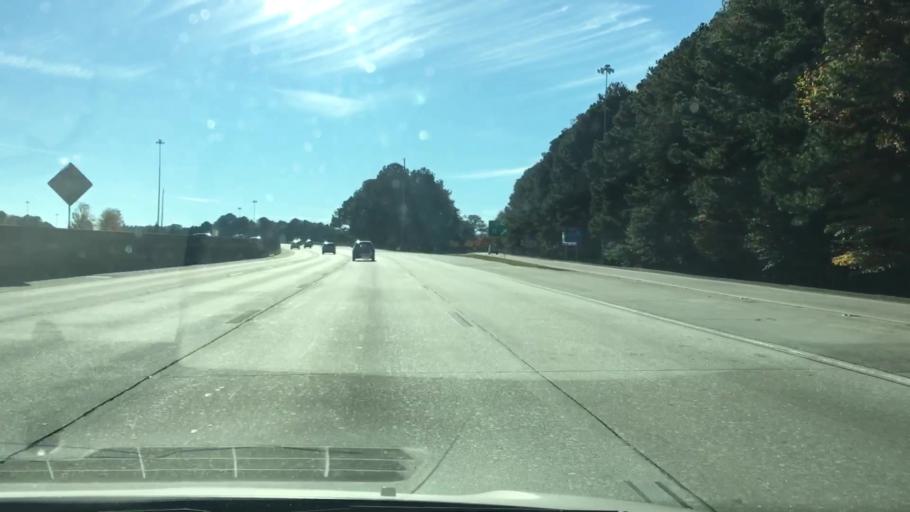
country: US
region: Georgia
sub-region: Fulton County
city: Alpharetta
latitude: 34.0916
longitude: -84.2593
